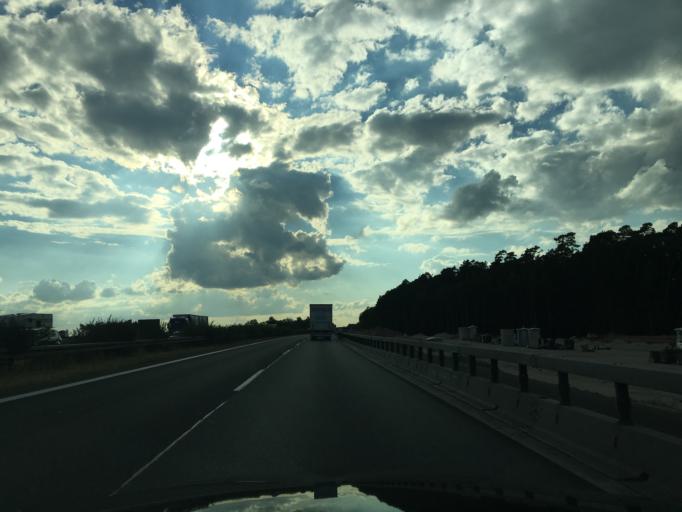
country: DE
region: Bavaria
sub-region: Regierungsbezirk Mittelfranken
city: Burgoberbach
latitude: 49.2598
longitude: 10.5471
